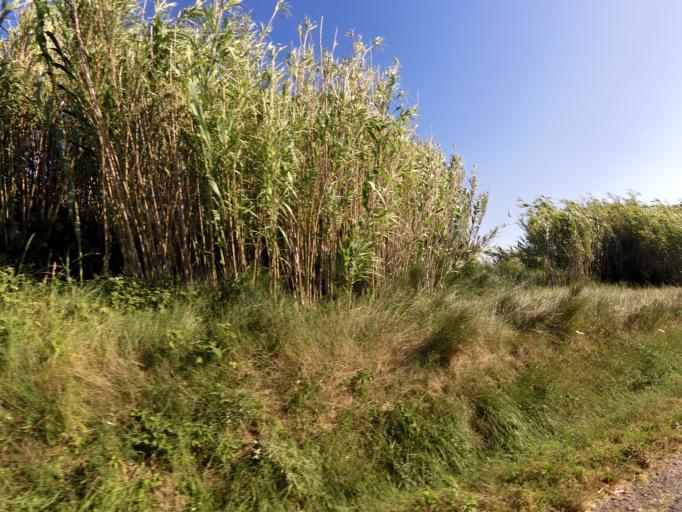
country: FR
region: Languedoc-Roussillon
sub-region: Departement de l'Herault
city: Boisseron
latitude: 43.7689
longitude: 4.0629
